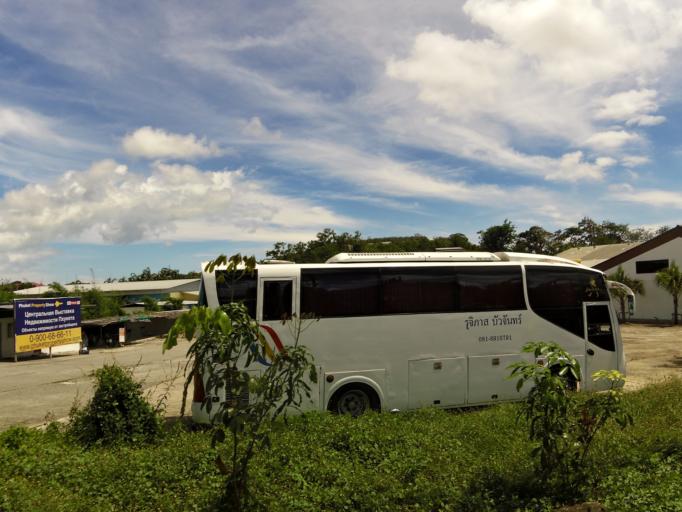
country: TH
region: Phuket
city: Mueang Phuket
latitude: 7.8629
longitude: 98.3454
